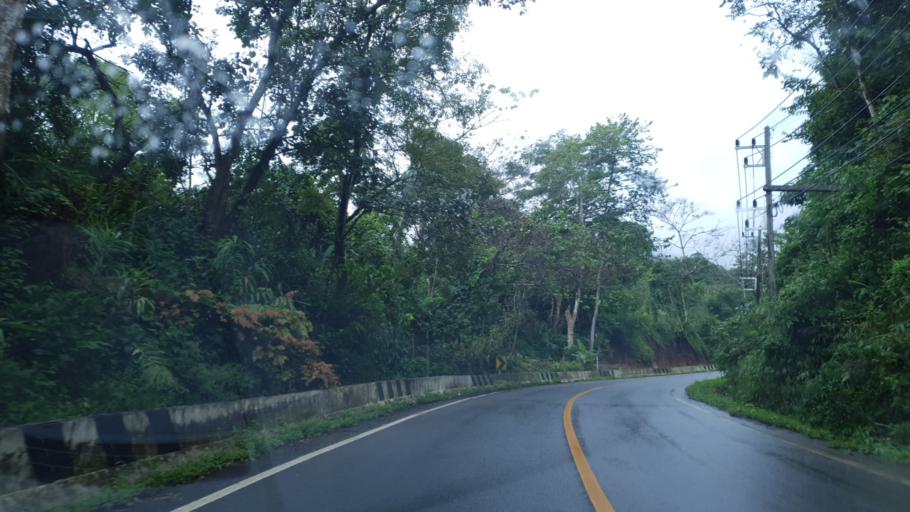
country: TH
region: Mae Hong Son
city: Pa Pae
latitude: 18.1682
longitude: 98.0653
